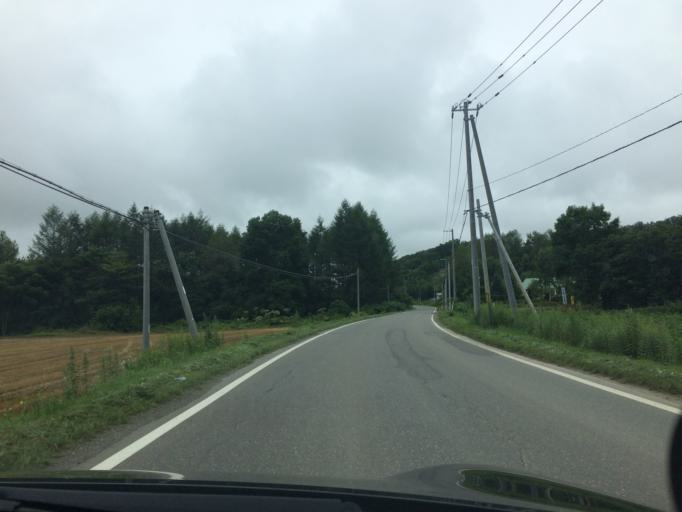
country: JP
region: Hokkaido
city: Otofuke
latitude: 42.9577
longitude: 143.1287
